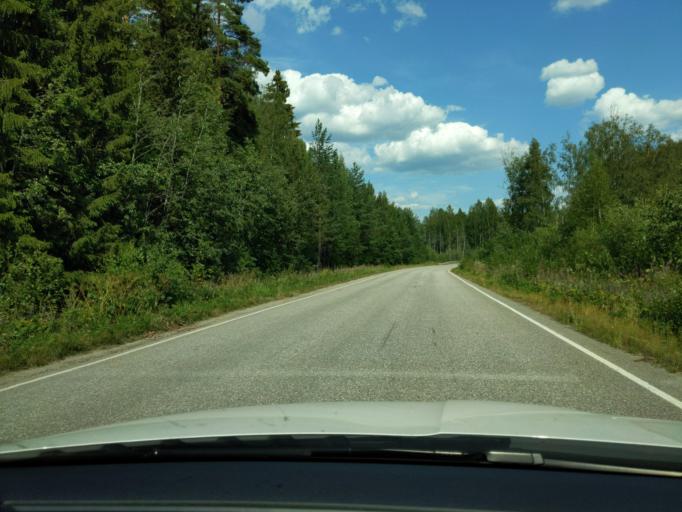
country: FI
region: Paijanne Tavastia
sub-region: Lahti
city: Heinola
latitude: 61.3349
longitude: 26.1682
